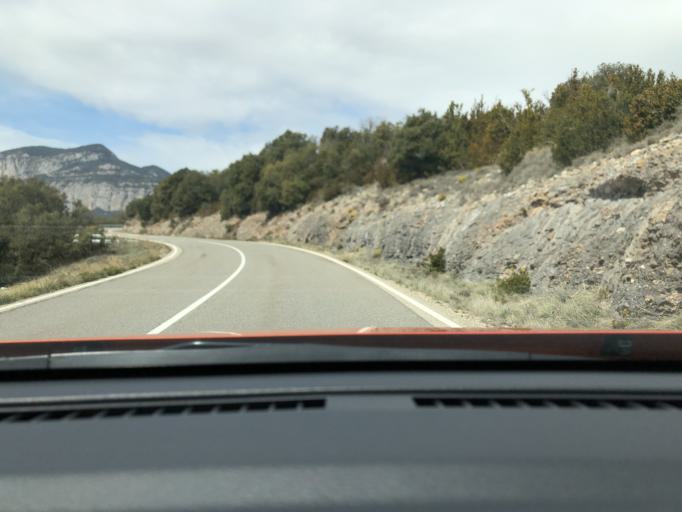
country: ES
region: Catalonia
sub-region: Provincia de Lleida
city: Olius
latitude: 42.1130
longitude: 1.5464
